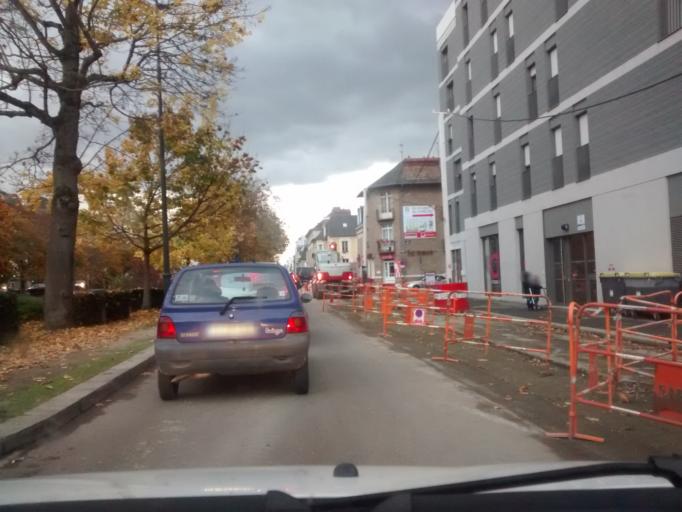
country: FR
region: Brittany
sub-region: Departement d'Ille-et-Vilaine
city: Rennes
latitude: 48.1099
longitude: -1.6675
